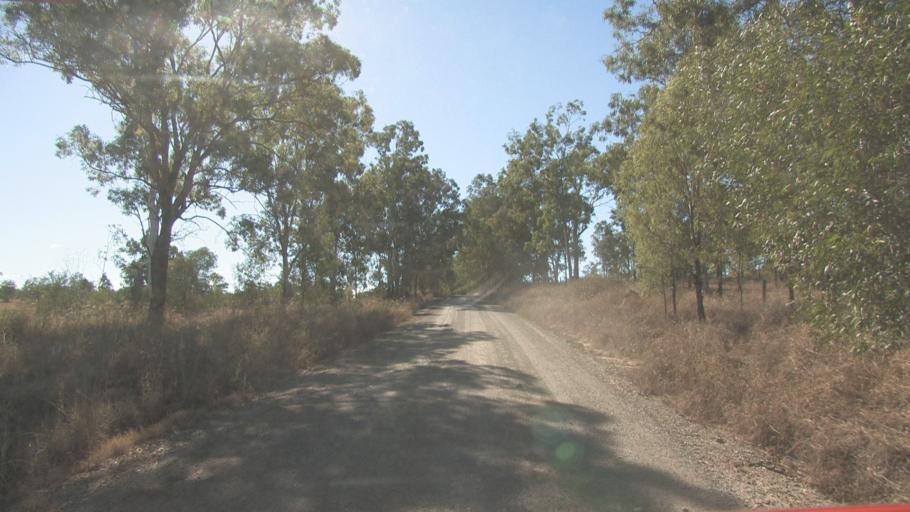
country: AU
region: Queensland
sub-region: Logan
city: Cedar Vale
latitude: -27.8491
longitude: 152.8953
